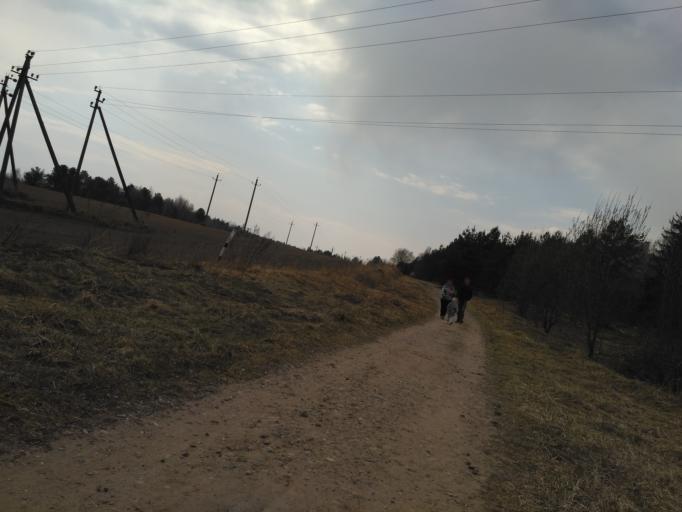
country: BY
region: Minsk
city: Zamostochcha
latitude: 53.8829
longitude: 27.9115
